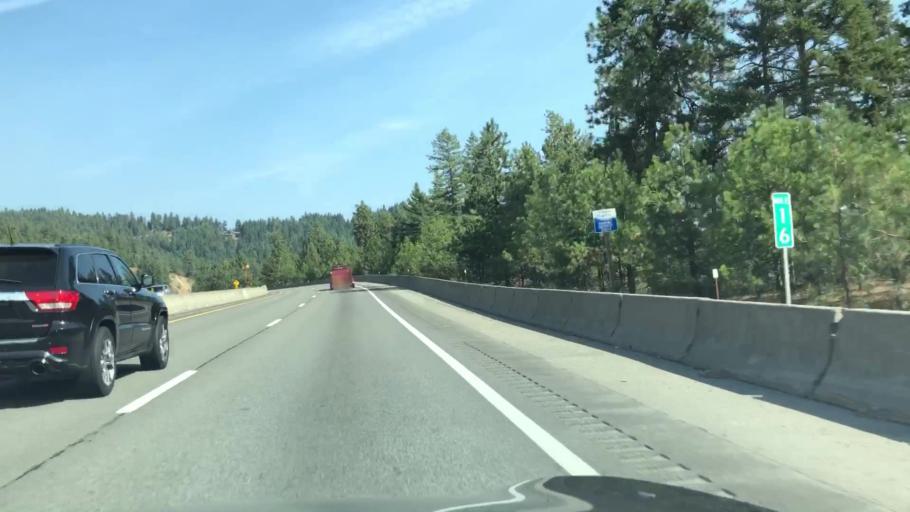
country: US
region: Idaho
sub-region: Kootenai County
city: Coeur d'Alene
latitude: 47.6624
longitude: -116.7382
